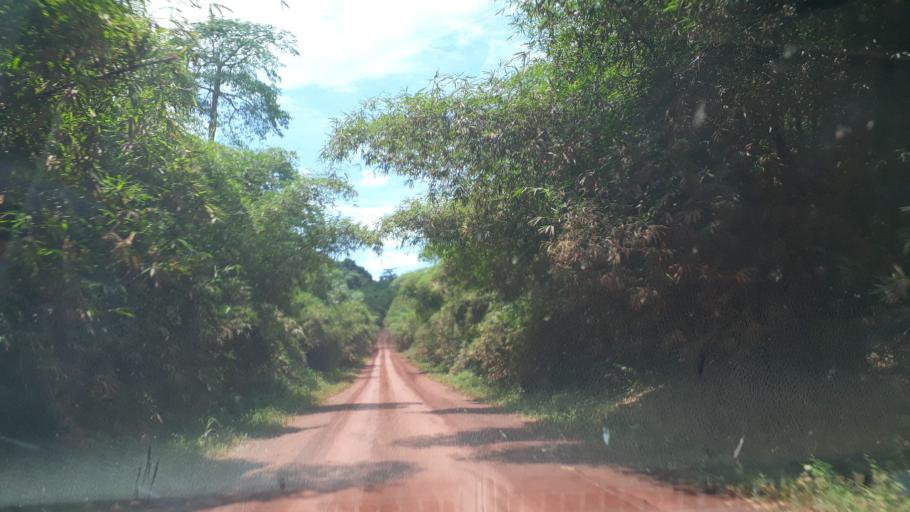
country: CD
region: Eastern Province
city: Kisangani
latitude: 0.6166
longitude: 26.0255
